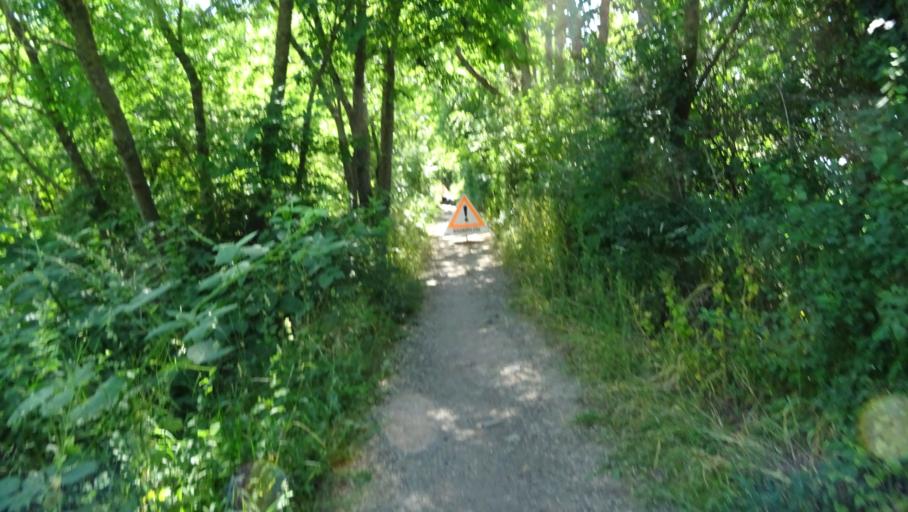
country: DE
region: Baden-Wuerttemberg
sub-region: Regierungsbezirk Stuttgart
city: Untereisesheim
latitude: 49.2279
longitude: 9.1994
